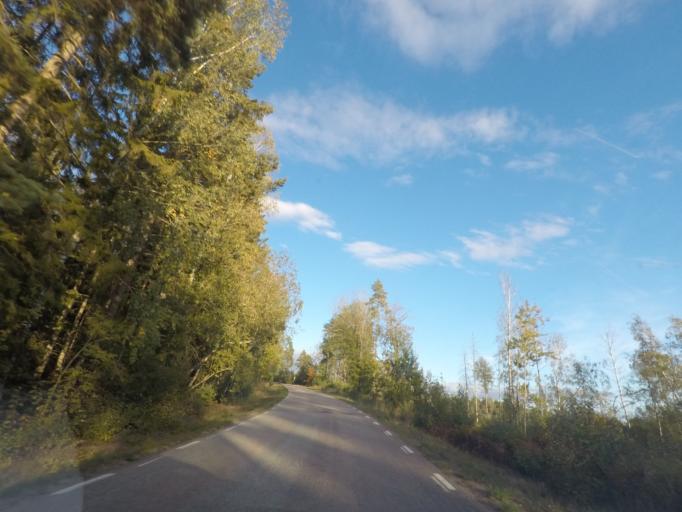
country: SE
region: Vaestmanland
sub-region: Kopings Kommun
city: Koping
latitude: 59.5097
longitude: 16.0761
